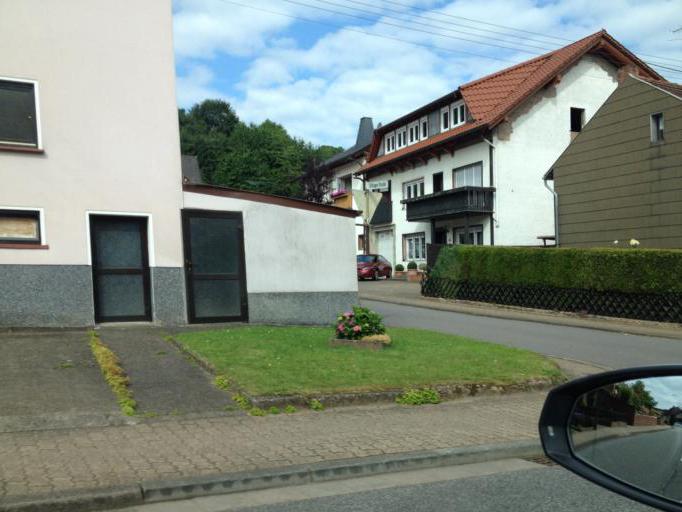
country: DE
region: Saarland
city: Losheim
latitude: 49.4848
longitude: 6.7824
